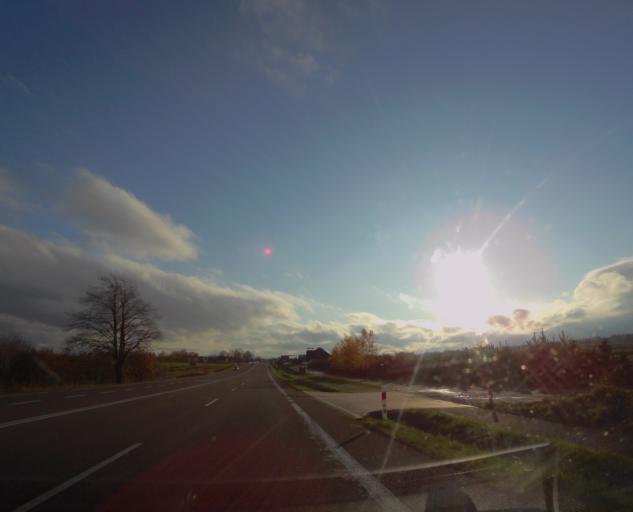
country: PL
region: Subcarpathian Voivodeship
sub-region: Powiat przemyski
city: Orly
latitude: 49.8502
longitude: 22.8040
